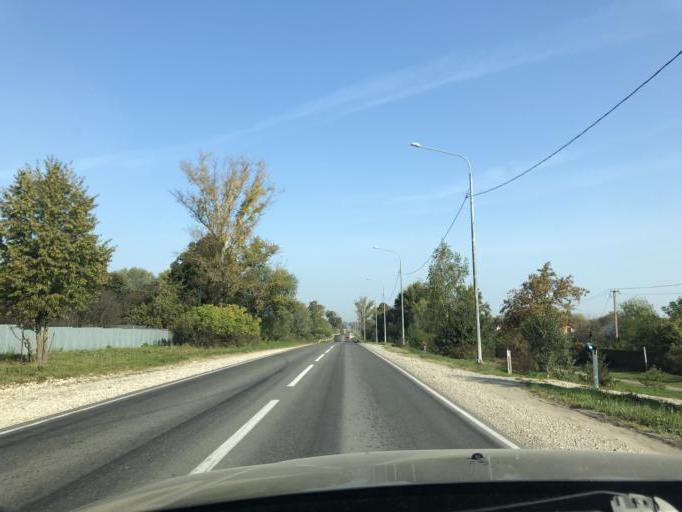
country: RU
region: Tula
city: Novogurovskiy
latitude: 54.4615
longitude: 37.4742
